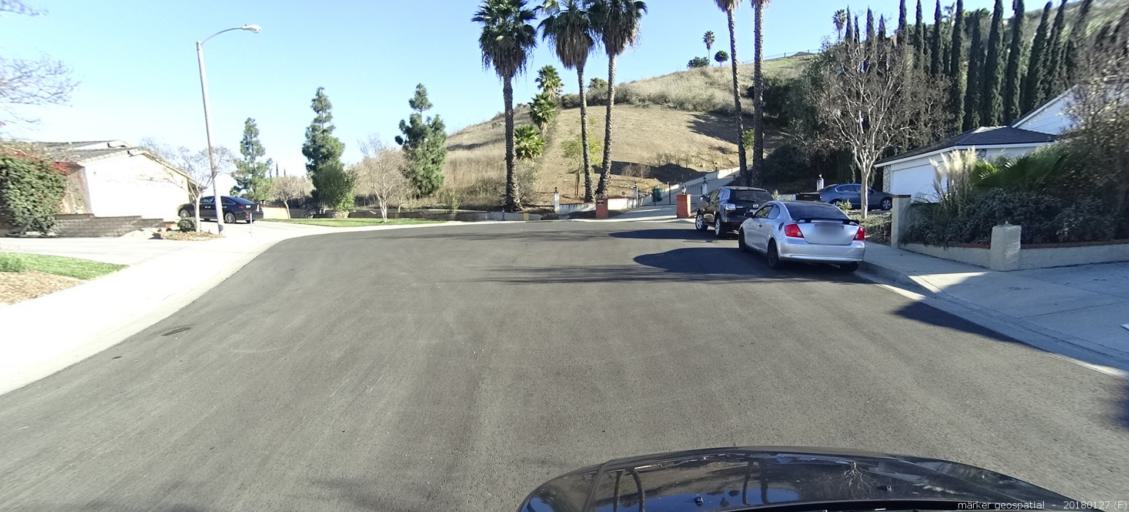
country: US
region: California
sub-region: Los Angeles County
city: Diamond Bar
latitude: 34.0226
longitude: -117.7920
